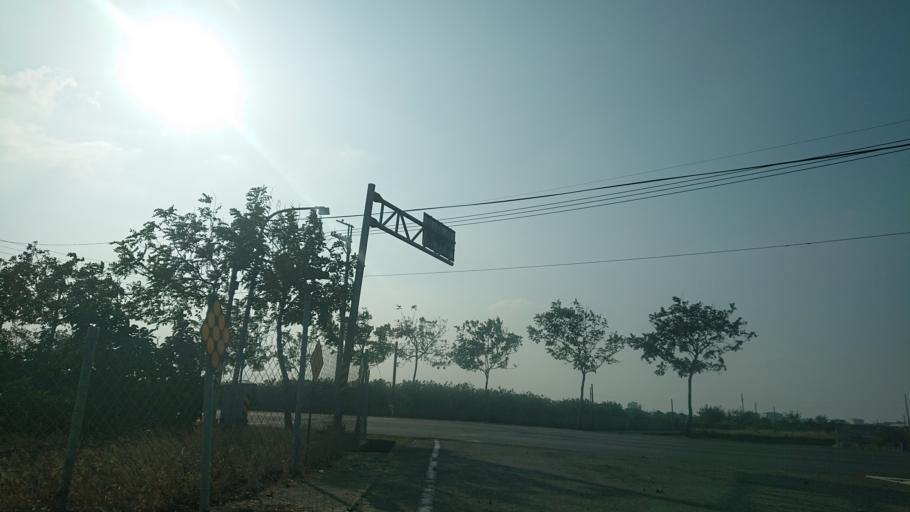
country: TW
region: Taiwan
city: Xinying
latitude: 23.2039
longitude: 120.2710
